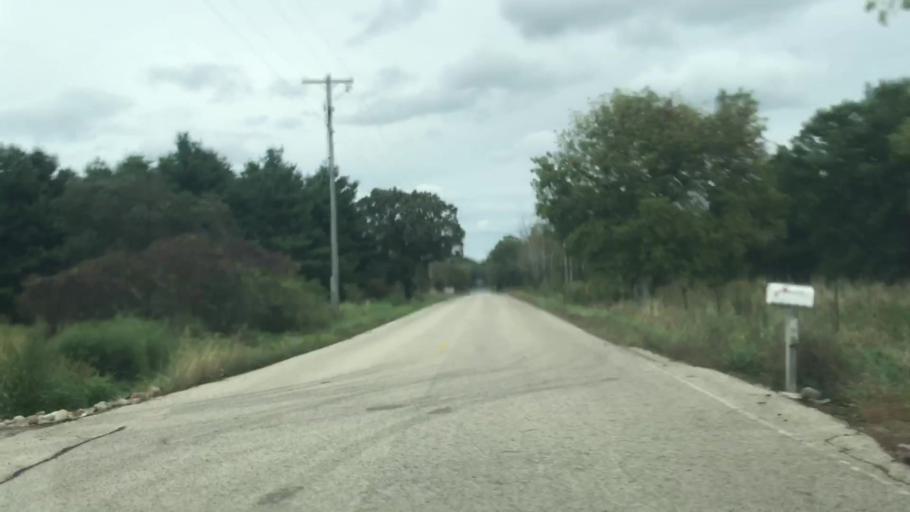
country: US
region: Wisconsin
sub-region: Waukesha County
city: North Prairie
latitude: 42.9152
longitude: -88.4286
